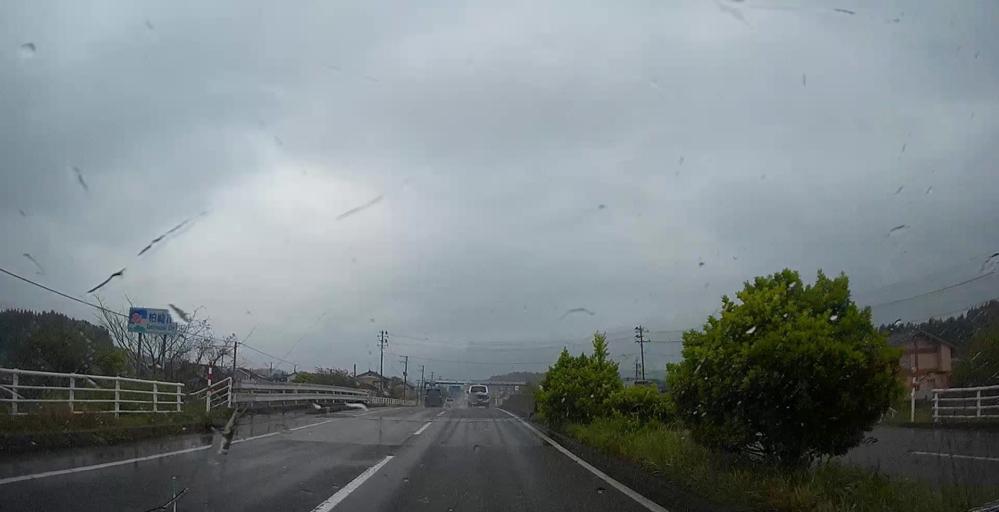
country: JP
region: Niigata
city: Kashiwazaki
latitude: 37.4461
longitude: 138.6379
